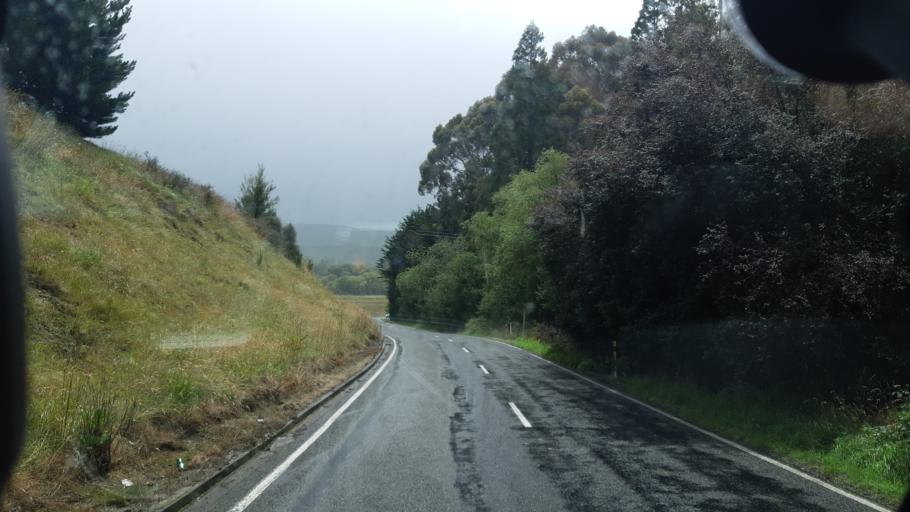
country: NZ
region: Canterbury
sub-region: Timaru District
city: Pleasant Point
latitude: -44.3127
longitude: 170.9462
